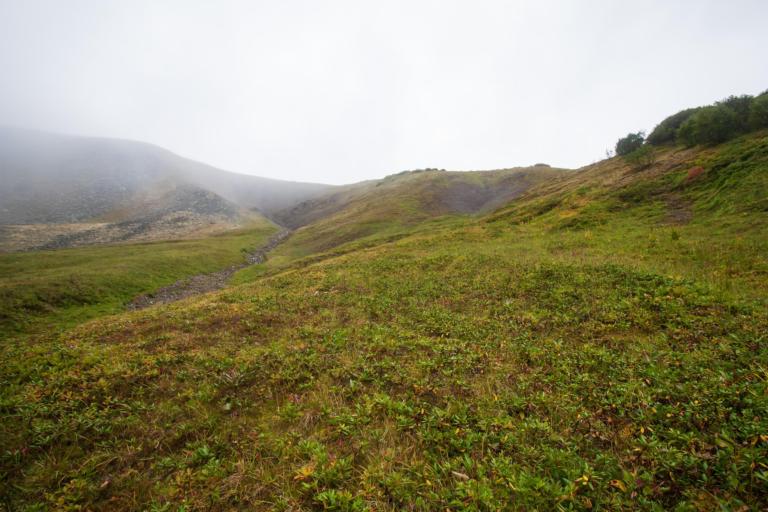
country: RU
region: Kamtsjatka
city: Yelizovo
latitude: 53.9771
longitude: 158.0828
